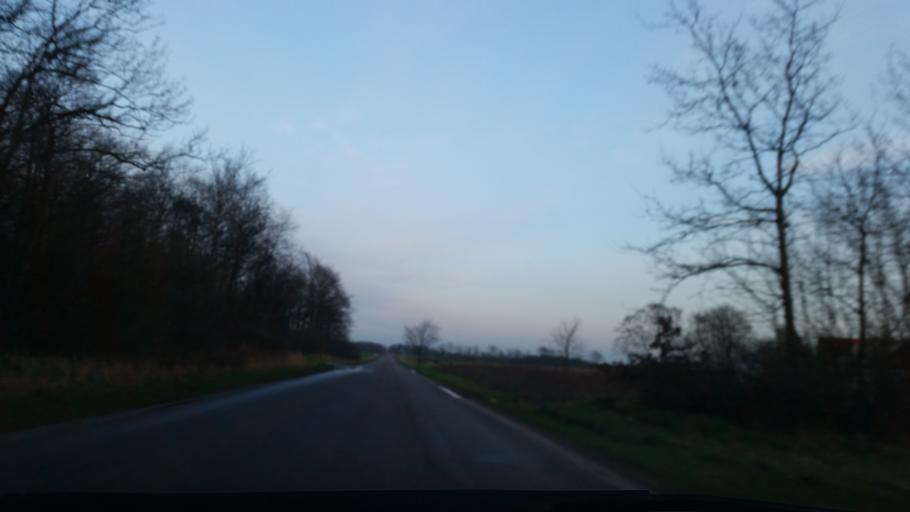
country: DK
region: South Denmark
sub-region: Vejen Kommune
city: Rodding
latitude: 55.3836
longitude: 8.9616
